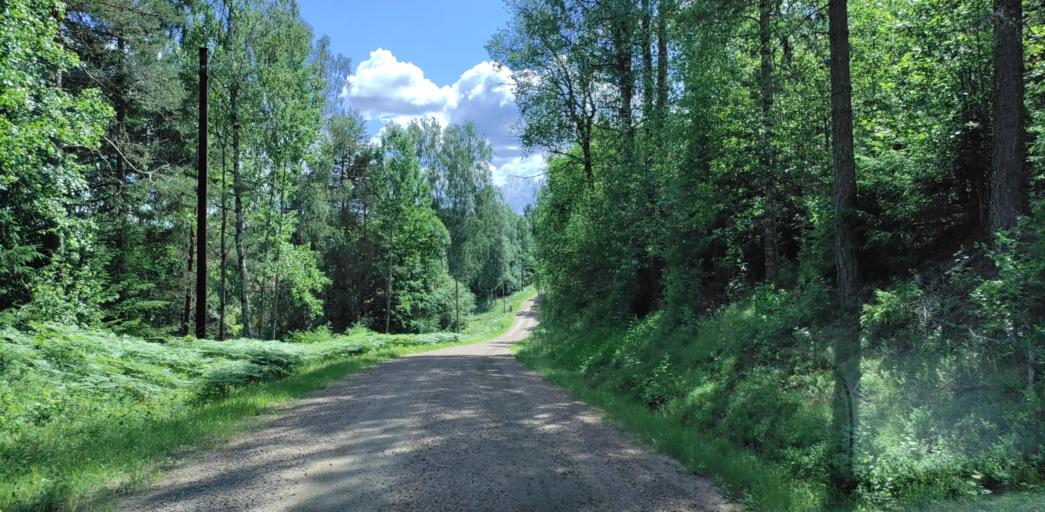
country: SE
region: Vaermland
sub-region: Munkfors Kommun
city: Munkfors
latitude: 59.9665
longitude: 13.5219
